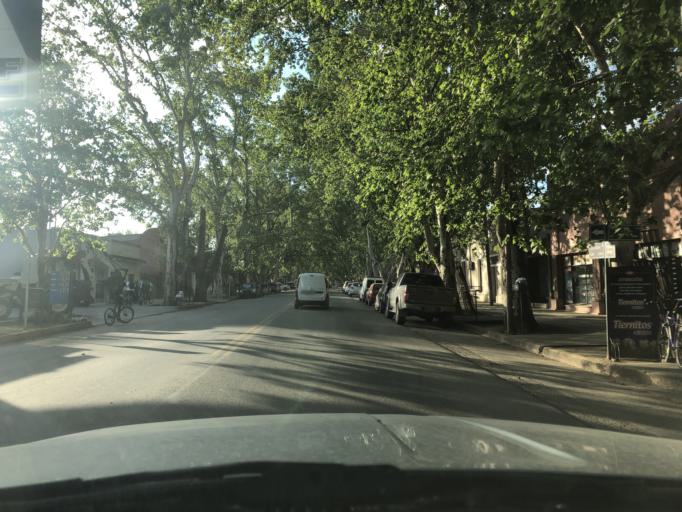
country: AR
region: Cordoba
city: Jesus Maria
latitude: -31.0195
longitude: -64.0639
